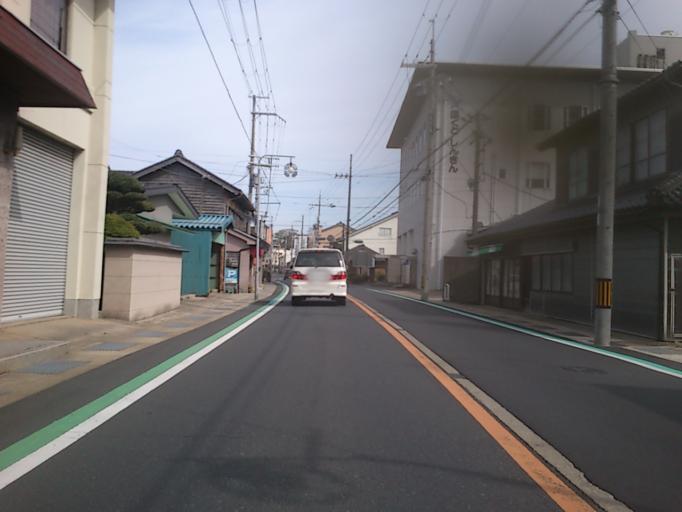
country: JP
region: Kyoto
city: Miyazu
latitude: 35.6827
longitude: 135.0263
